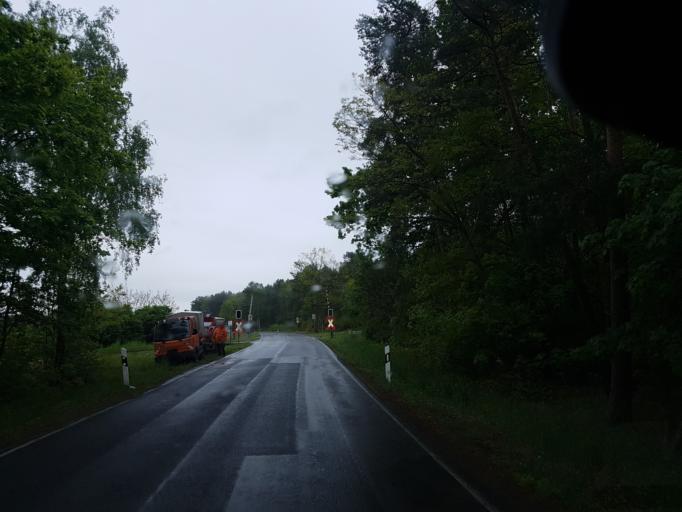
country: DE
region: Brandenburg
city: Spremberg
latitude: 51.6773
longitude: 14.4194
